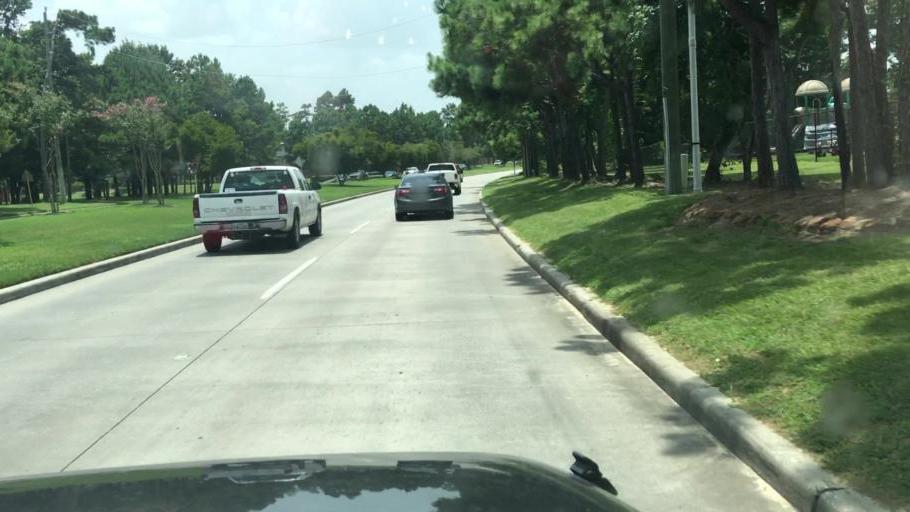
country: US
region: Texas
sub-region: Harris County
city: Atascocita
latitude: 29.9610
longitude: -95.1687
